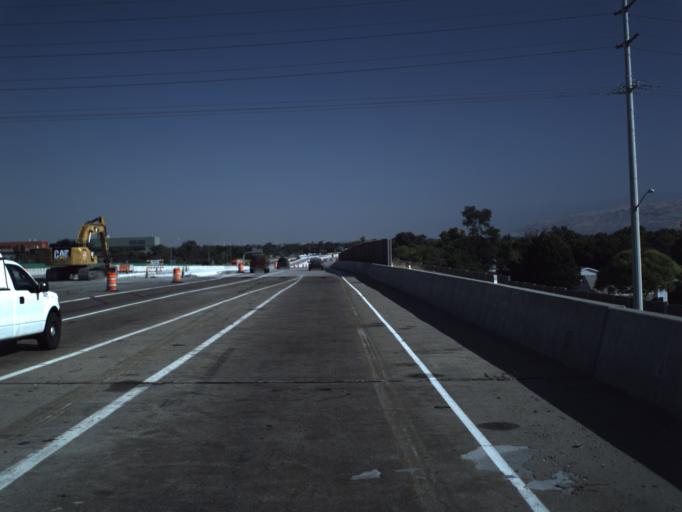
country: US
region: Utah
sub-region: Salt Lake County
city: Taylorsville
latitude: 40.6672
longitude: -111.9523
